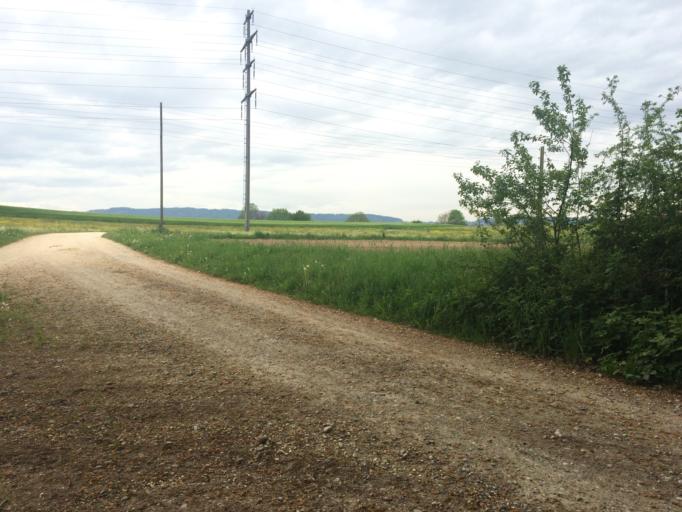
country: CH
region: Zurich
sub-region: Bezirk Uster
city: Uster / Ober-Uster
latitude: 47.3405
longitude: 8.7451
